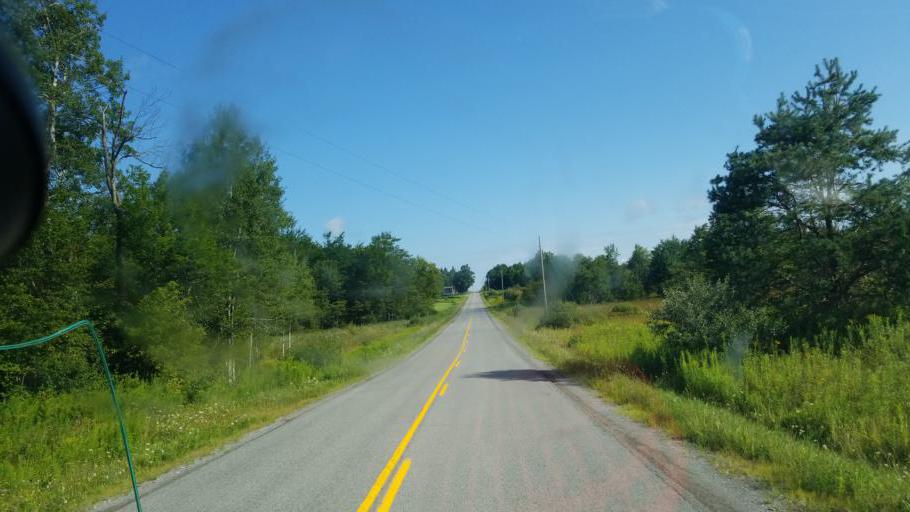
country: US
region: New York
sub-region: Allegany County
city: Andover
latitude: 42.1650
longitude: -77.7132
